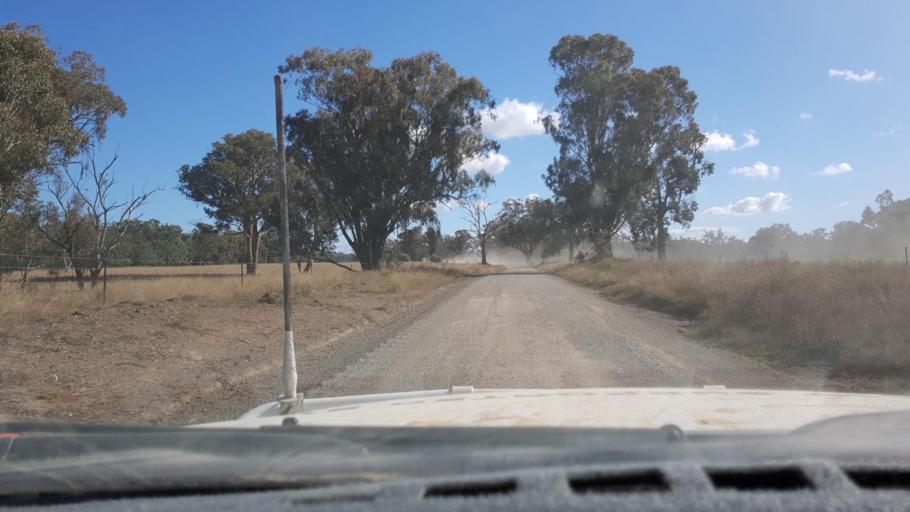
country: AU
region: New South Wales
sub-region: Tamworth Municipality
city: Manilla
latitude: -30.5937
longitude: 150.4938
